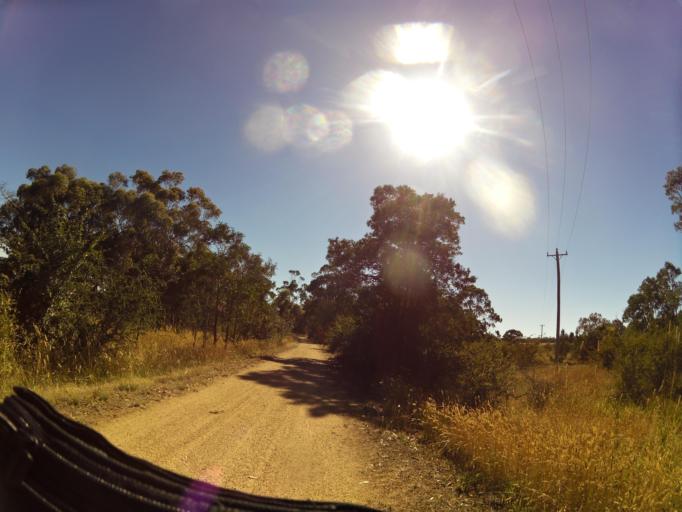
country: AU
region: Victoria
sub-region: Ballarat North
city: Delacombe
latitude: -37.6816
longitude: 143.4322
